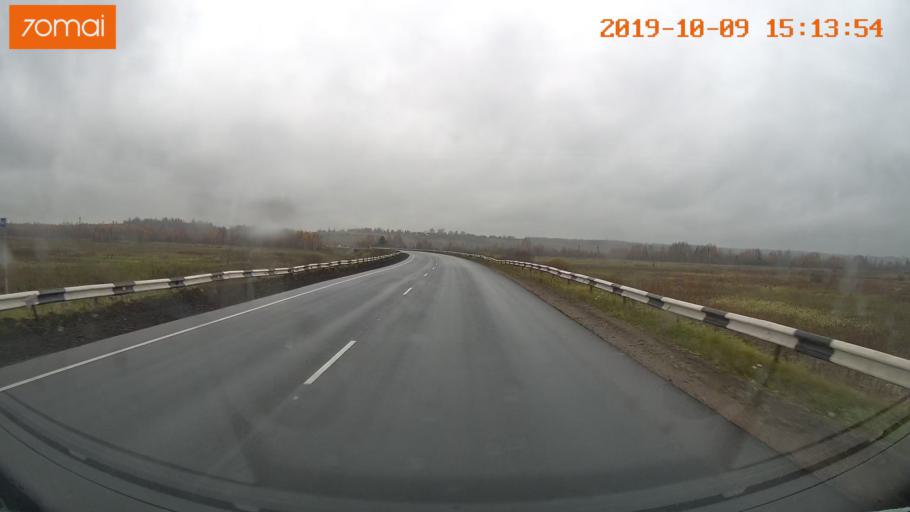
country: RU
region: Kostroma
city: Susanino
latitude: 58.1430
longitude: 41.6117
